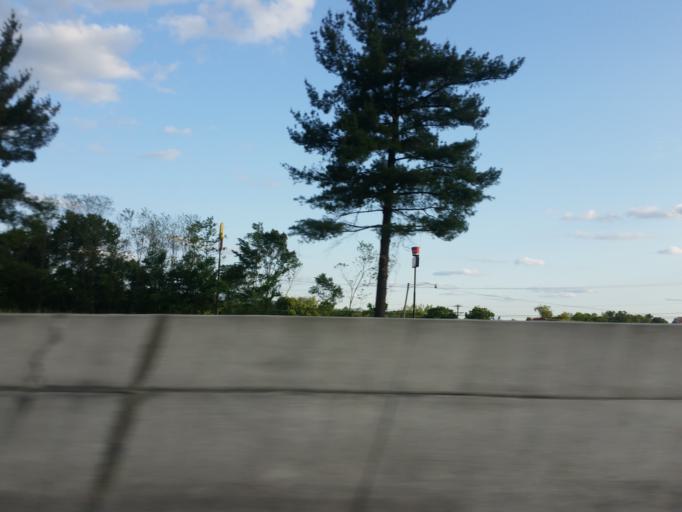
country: US
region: Virginia
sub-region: City of Bristol
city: Bristol
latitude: 36.6264
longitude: -82.1599
